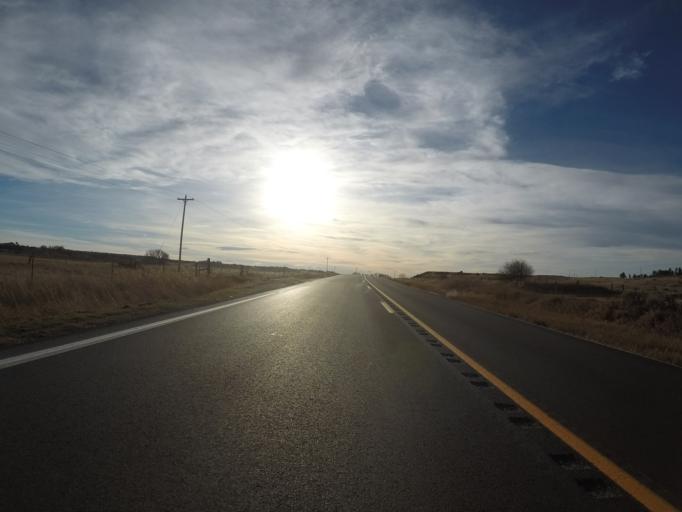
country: US
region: Montana
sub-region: Musselshell County
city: Roundup
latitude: 46.3733
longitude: -108.6401
